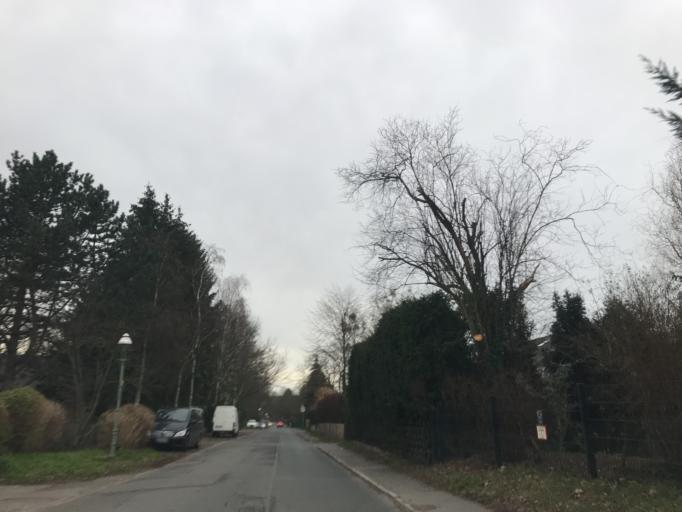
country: DE
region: Berlin
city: Kladow
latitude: 52.4524
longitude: 13.1337
